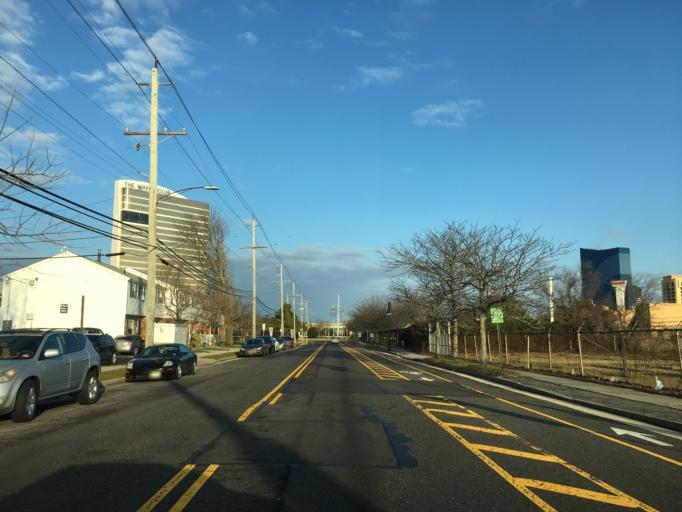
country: US
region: New Jersey
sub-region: Atlantic County
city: Atlantic City
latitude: 39.3753
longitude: -74.4289
